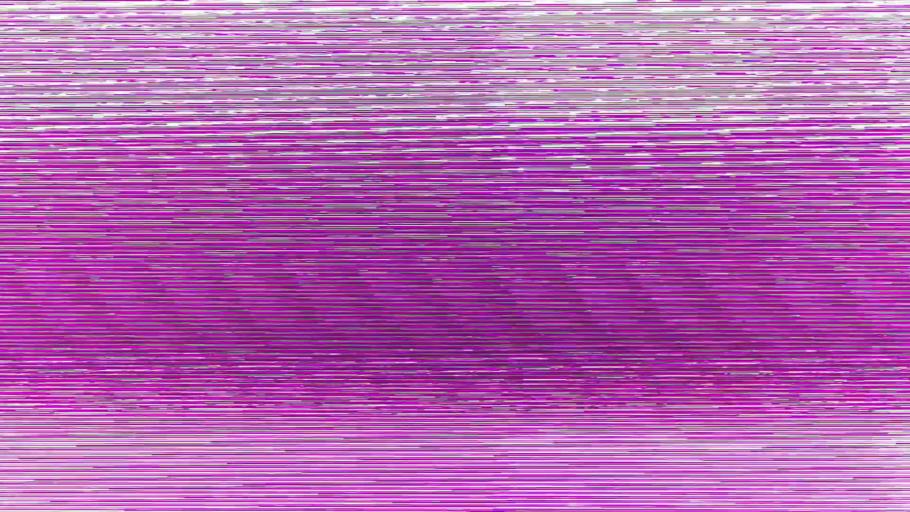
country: US
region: Michigan
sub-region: Washtenaw County
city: Ypsilanti
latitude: 42.2371
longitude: -83.6131
